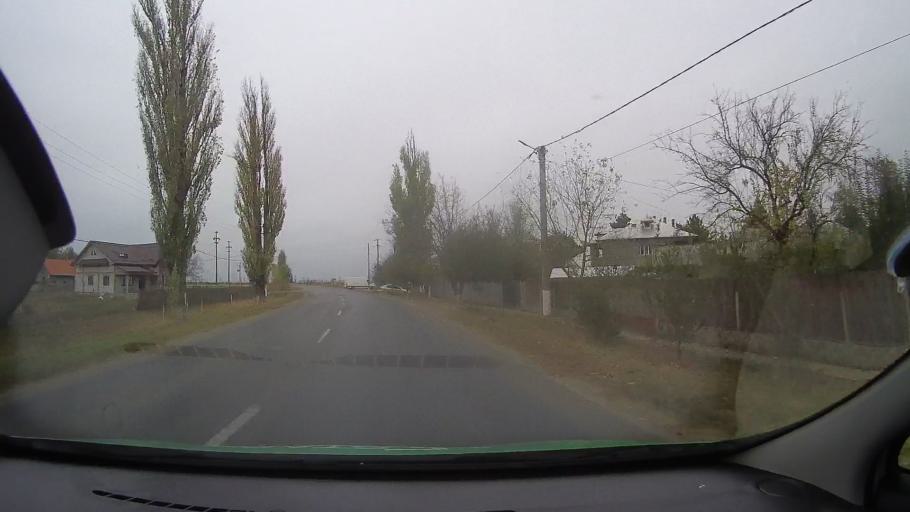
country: RO
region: Ialomita
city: Tandarei
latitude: 44.6552
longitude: 27.6535
